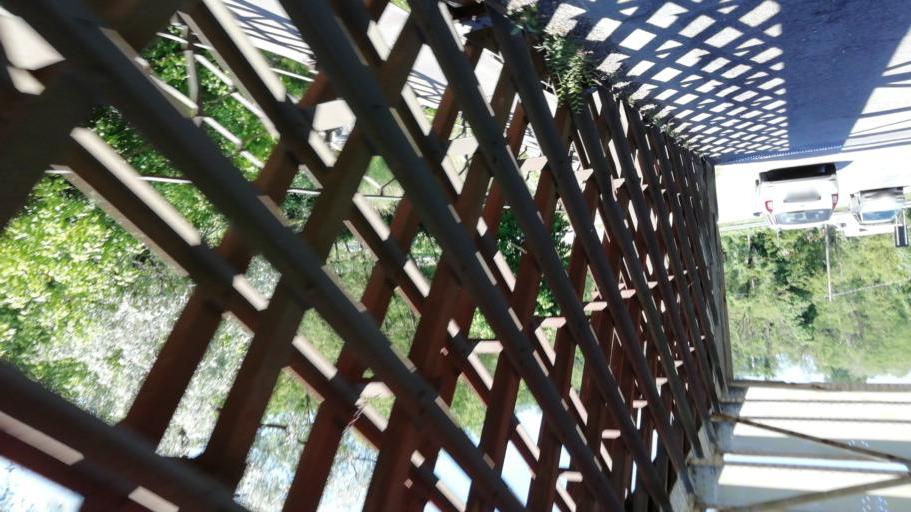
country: IT
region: Lombardy
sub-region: Provincia di Varese
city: Vizzola Ticino
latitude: 45.5894
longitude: 8.7053
